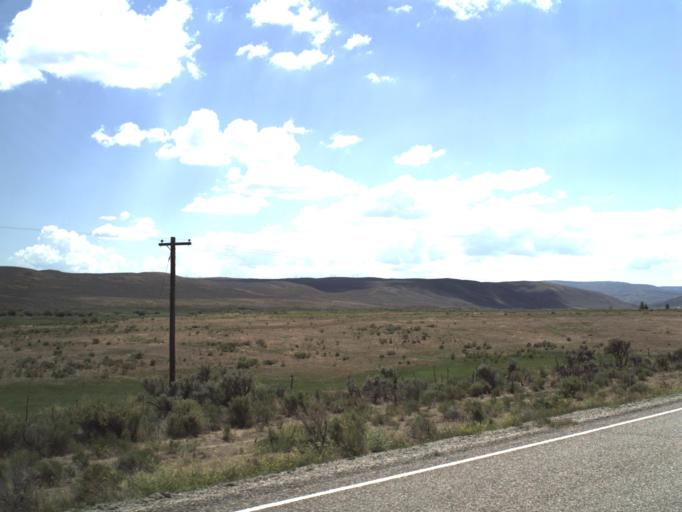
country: US
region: Utah
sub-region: Rich County
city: Randolph
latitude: 41.5199
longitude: -111.1999
